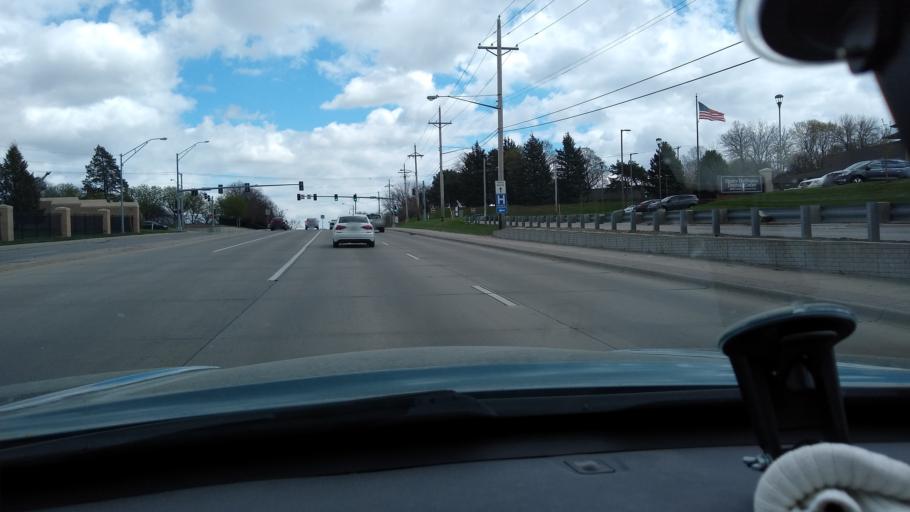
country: US
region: Nebraska
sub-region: Douglas County
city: Ralston
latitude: 41.2342
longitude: -96.0350
